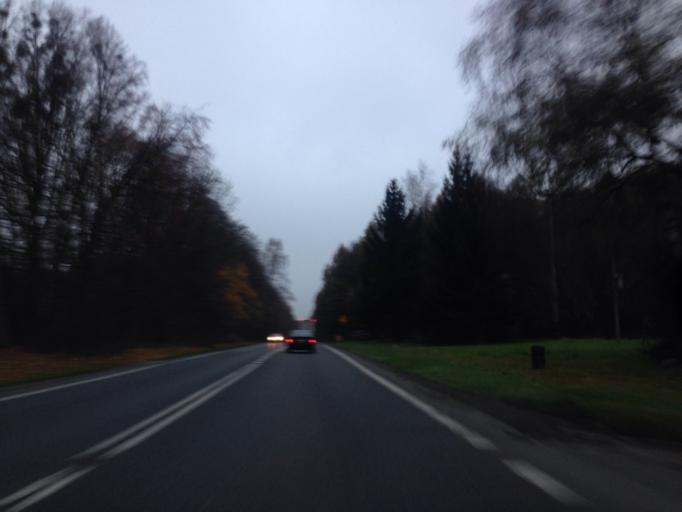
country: PL
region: Lodz Voivodeship
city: Lodz
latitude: 51.8237
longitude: 19.5168
